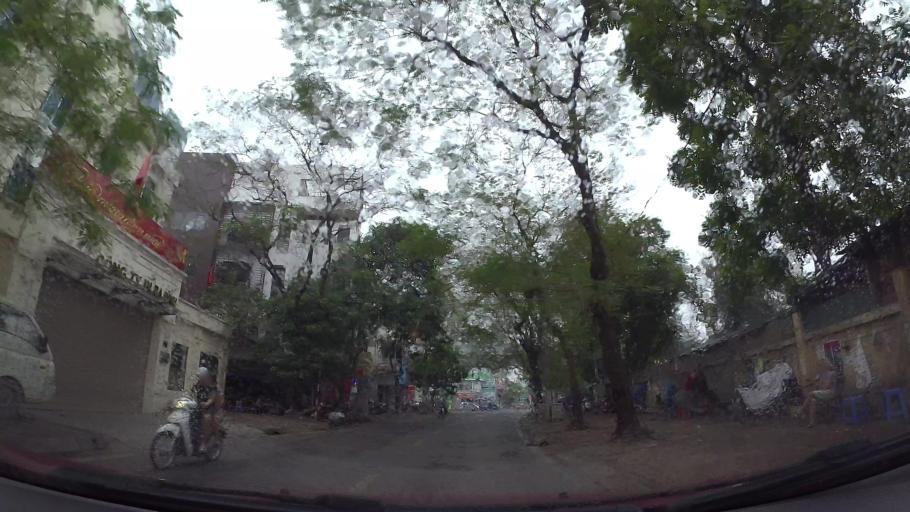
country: VN
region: Ha Noi
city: Dong Da
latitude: 21.0126
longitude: 105.8168
